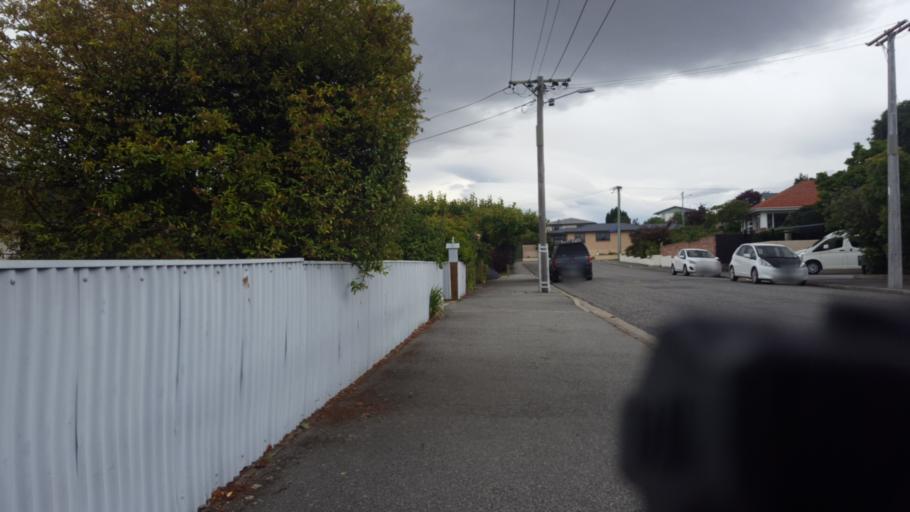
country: NZ
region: Otago
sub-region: Queenstown-Lakes District
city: Wanaka
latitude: -45.2518
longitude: 169.3972
